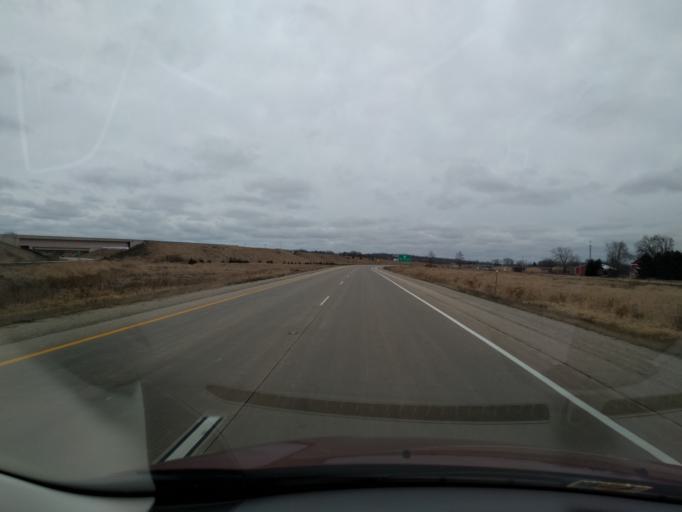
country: US
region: Wisconsin
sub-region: Winnebago County
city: Winneconne
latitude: 44.2090
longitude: -88.6873
